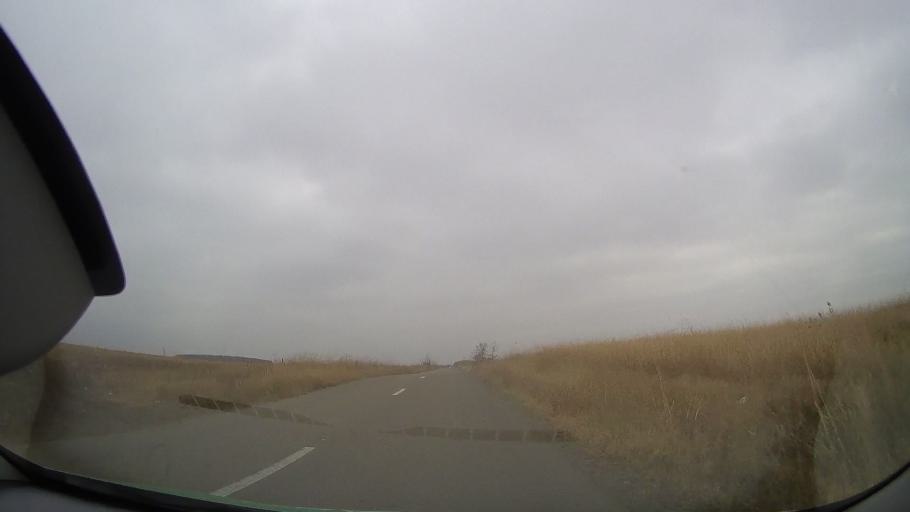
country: RO
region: Buzau
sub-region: Comuna Scutelnici
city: Scutelnici
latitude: 44.8713
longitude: 26.8876
